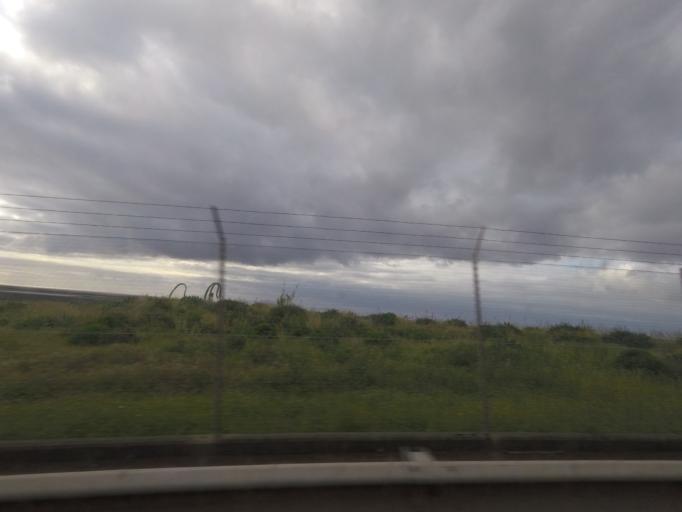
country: PT
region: Madeira
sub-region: Machico
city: Machico
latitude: 32.7051
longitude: -16.7681
